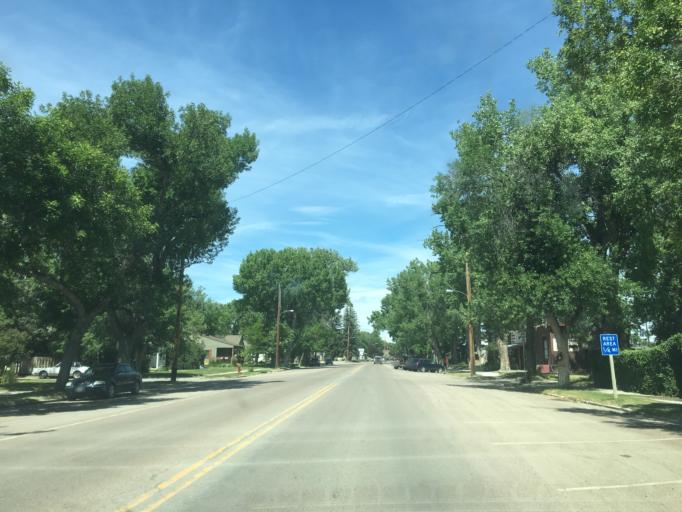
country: US
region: Montana
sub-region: Teton County
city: Choteau
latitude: 47.8156
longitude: -112.1863
